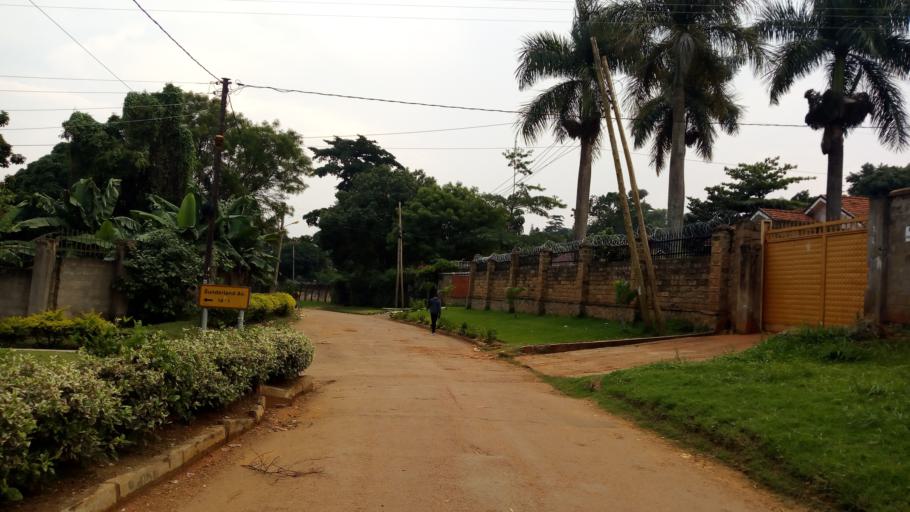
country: UG
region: Central Region
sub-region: Wakiso District
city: Kireka
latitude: 0.3214
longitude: 32.6293
